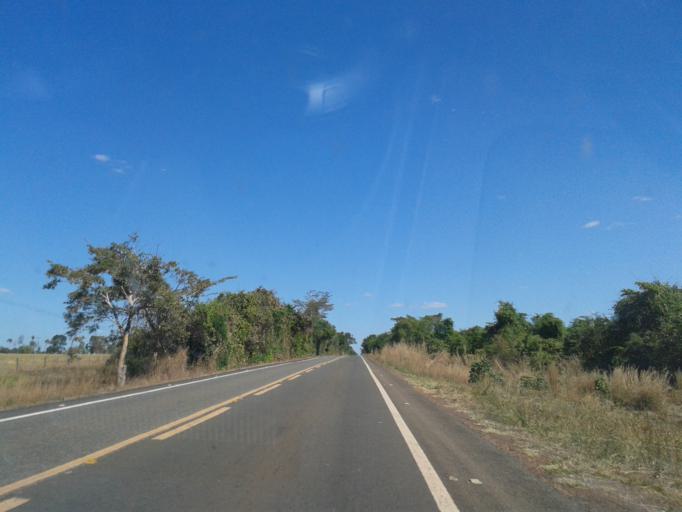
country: BR
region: Goias
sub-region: Sao Miguel Do Araguaia
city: Sao Miguel do Araguaia
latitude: -13.7134
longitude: -50.3335
